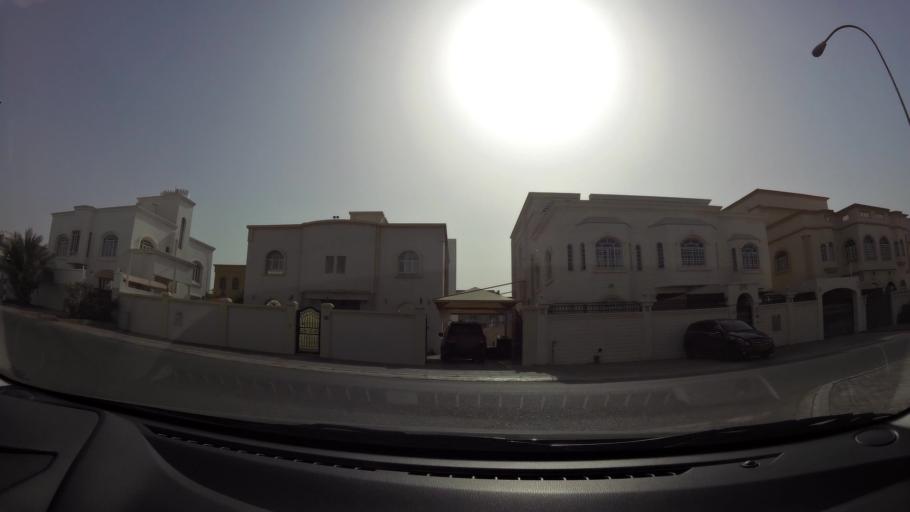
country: OM
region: Muhafazat Masqat
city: Bawshar
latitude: 23.5549
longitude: 58.3533
